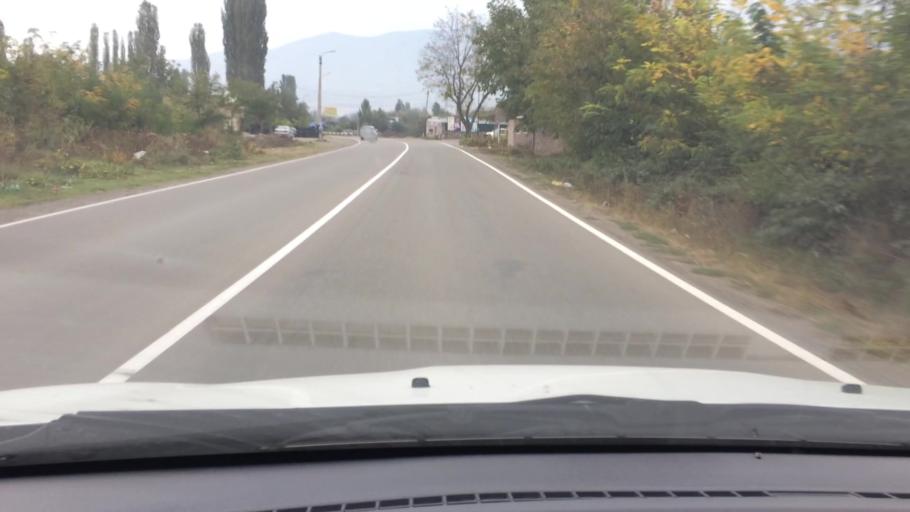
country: AM
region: Tavush
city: Bagratashen
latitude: 41.2573
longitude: 44.7974
